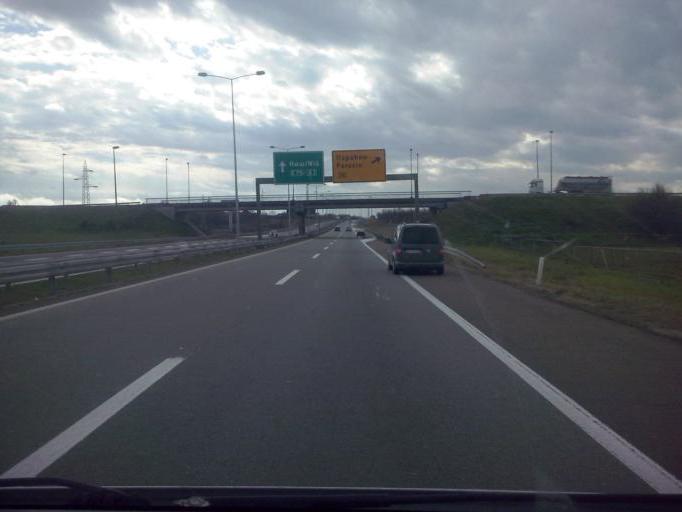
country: RS
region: Central Serbia
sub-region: Pomoravski Okrug
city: Paracin
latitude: 43.8581
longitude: 21.4368
